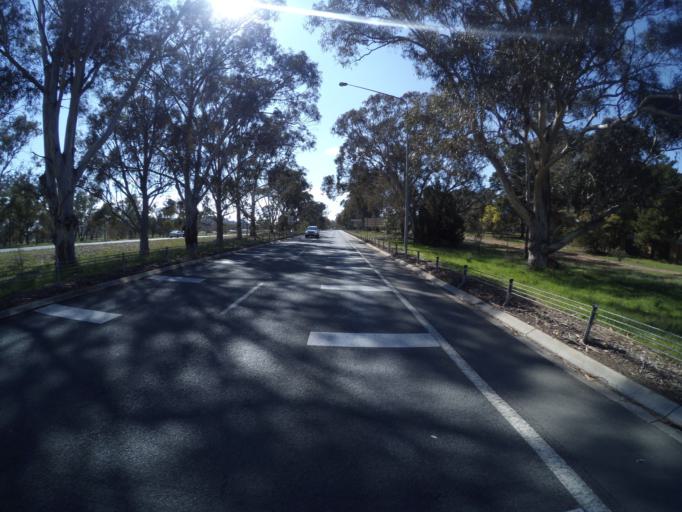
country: AU
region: Australian Capital Territory
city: Kaleen
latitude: -35.2239
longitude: 149.1682
